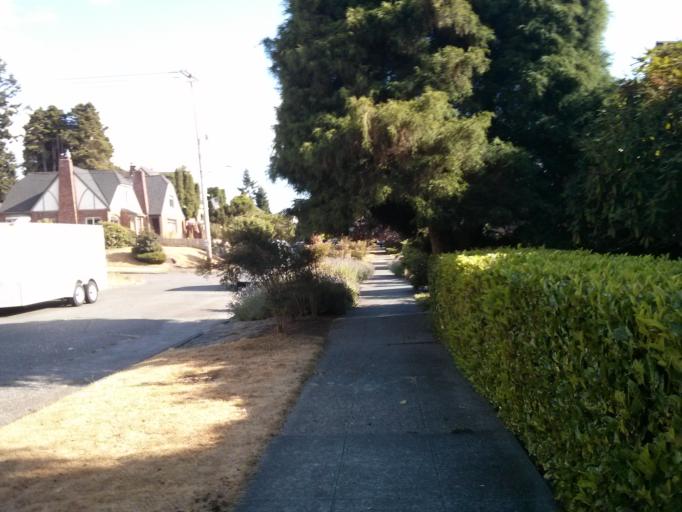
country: US
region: Washington
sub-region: King County
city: Seattle
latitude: 47.5858
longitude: -122.3919
